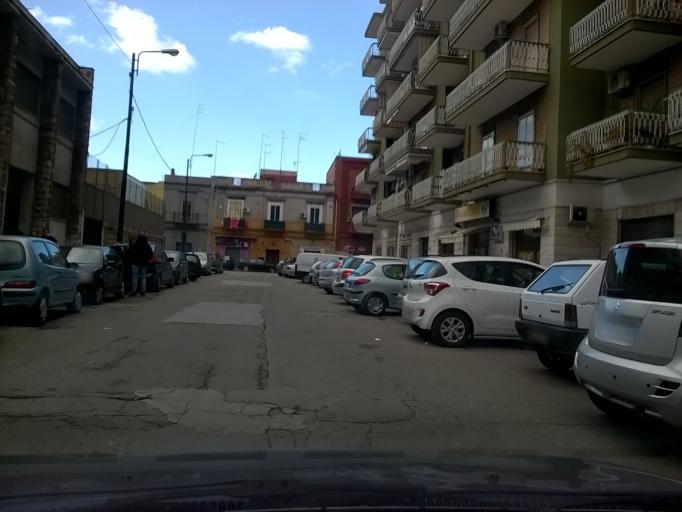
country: IT
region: Apulia
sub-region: Provincia di Taranto
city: Statte
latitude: 40.4885
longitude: 17.2282
